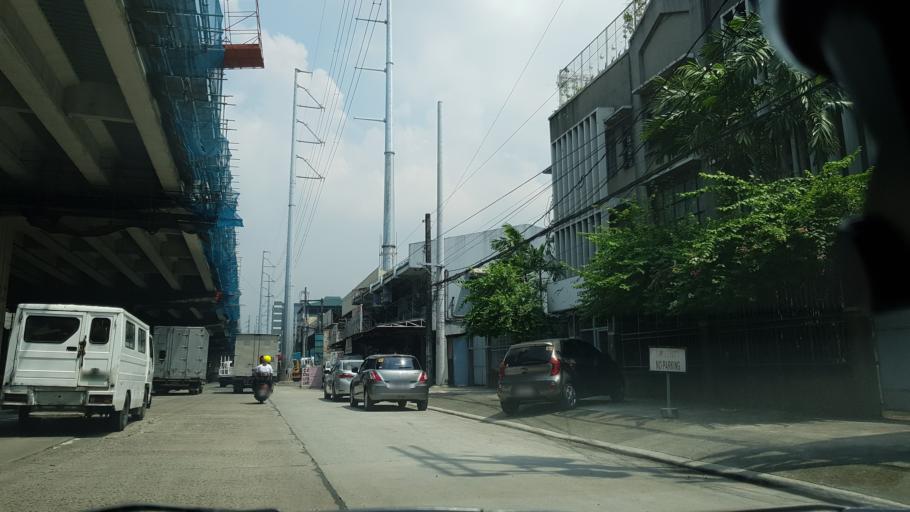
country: PH
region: Metro Manila
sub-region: San Juan
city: San Juan
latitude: 14.6093
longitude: 121.0172
